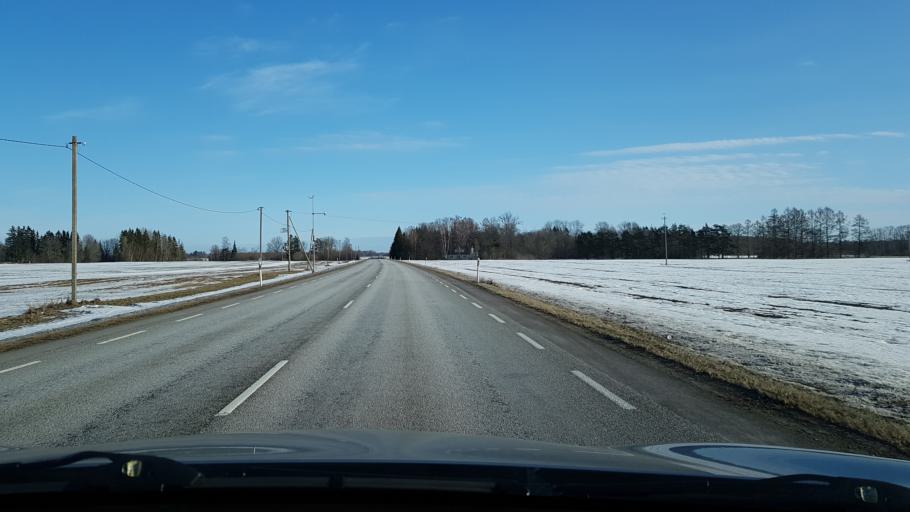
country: EE
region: Viljandimaa
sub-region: Vohma linn
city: Vohma
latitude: 58.6738
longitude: 25.6609
